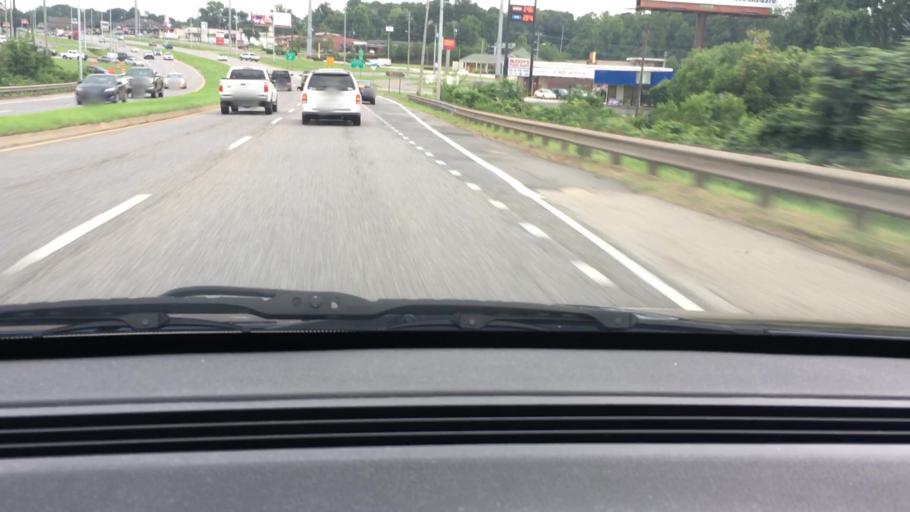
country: US
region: Alabama
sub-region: Tuscaloosa County
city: Tuscaloosa
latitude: 33.2265
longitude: -87.5327
